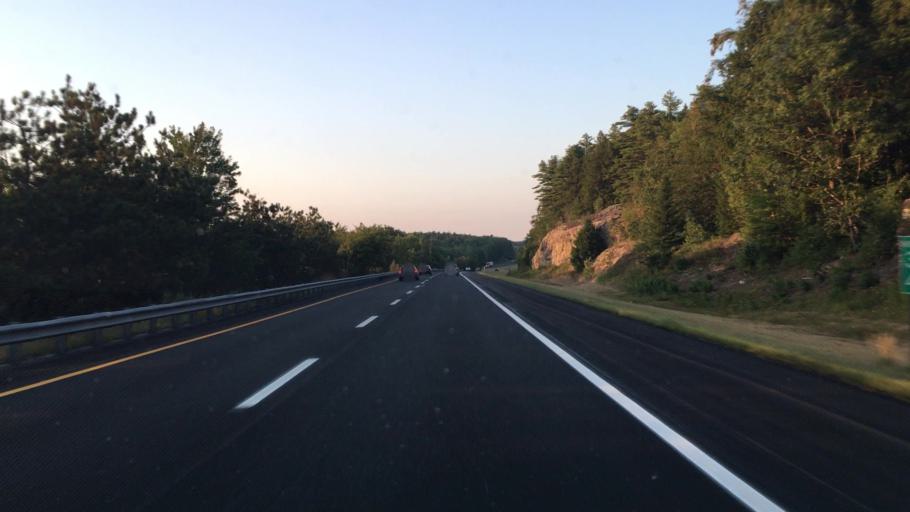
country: US
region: Maine
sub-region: Sagadahoc County
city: Topsham
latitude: 43.9768
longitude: -69.9457
